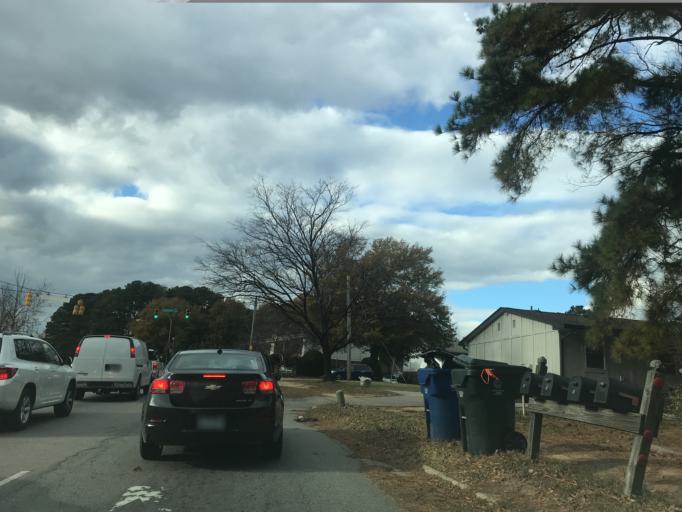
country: US
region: North Carolina
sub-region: Wake County
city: Raleigh
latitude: 35.8495
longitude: -78.5761
